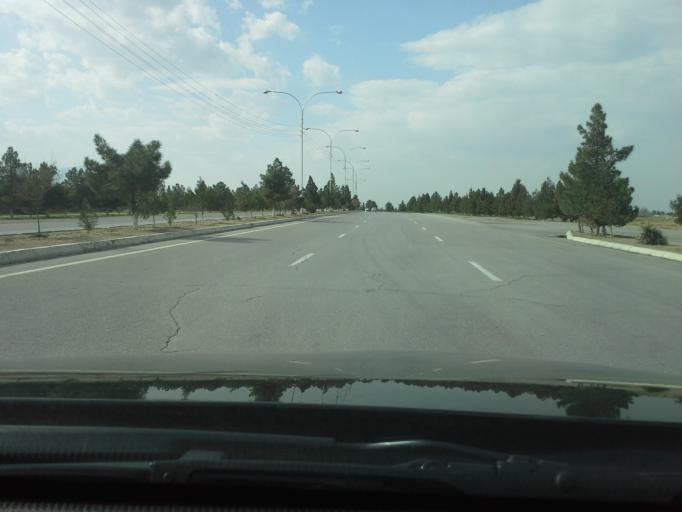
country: TM
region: Ahal
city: Ashgabat
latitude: 37.9679
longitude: 58.3016
